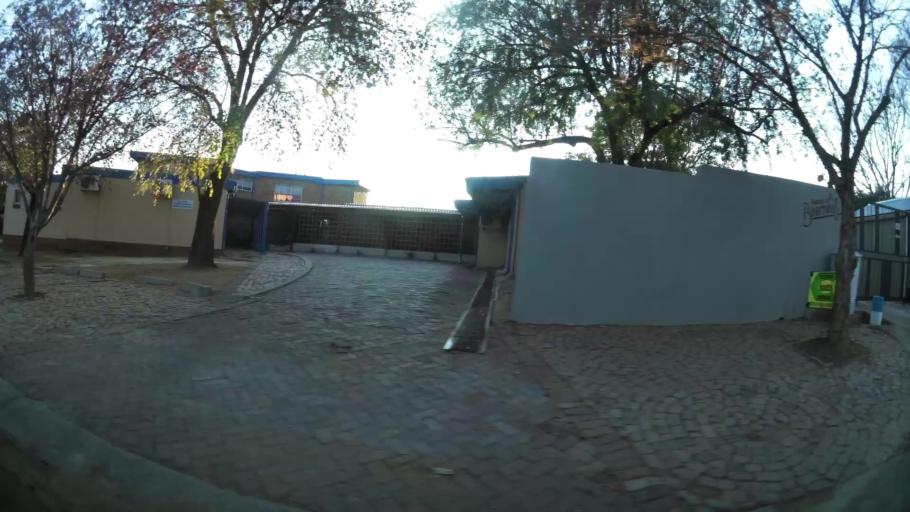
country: ZA
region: Orange Free State
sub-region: Mangaung Metropolitan Municipality
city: Bloemfontein
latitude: -29.0947
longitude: 26.1533
